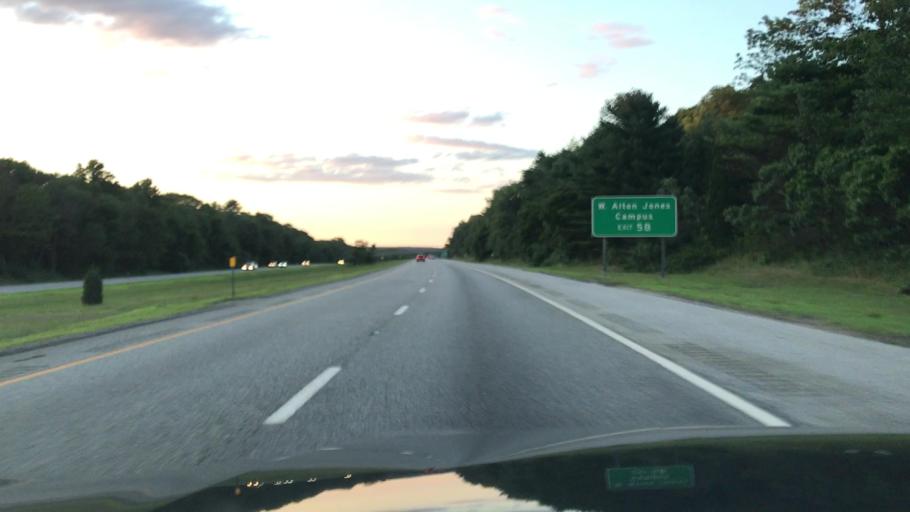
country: US
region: Rhode Island
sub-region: Kent County
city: West Greenwich
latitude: 41.5854
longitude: -71.6594
